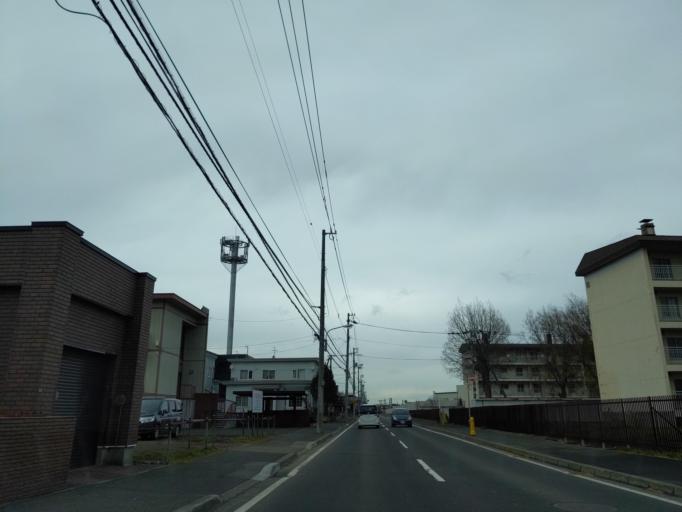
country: JP
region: Hokkaido
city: Sapporo
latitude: 43.0818
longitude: 141.3936
